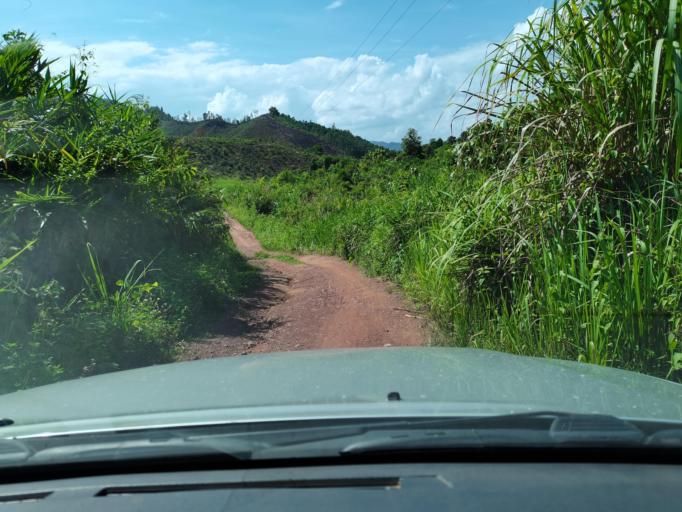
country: LA
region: Loungnamtha
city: Muang Nale
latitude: 20.5612
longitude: 101.0590
